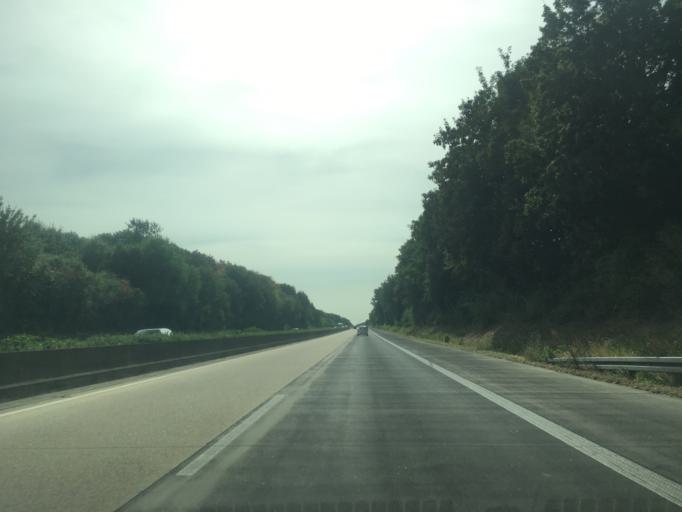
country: DE
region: North Rhine-Westphalia
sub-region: Regierungsbezirk Koln
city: Bedburg
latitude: 50.9851
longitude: 6.5557
